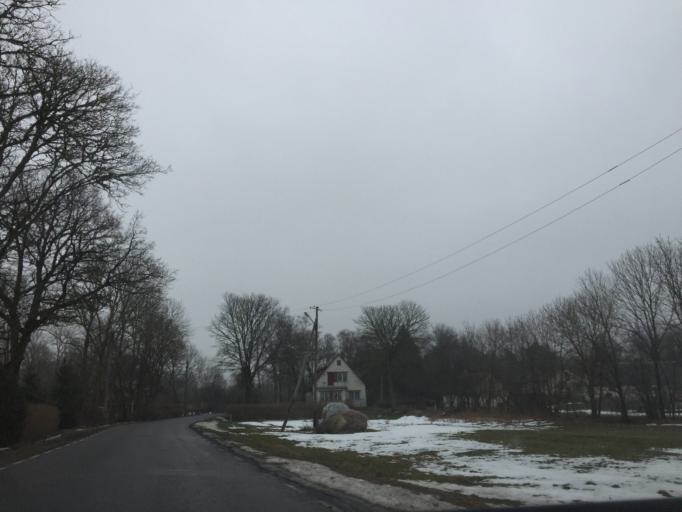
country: EE
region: Saare
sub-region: Orissaare vald
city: Orissaare
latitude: 58.4103
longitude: 22.8022
